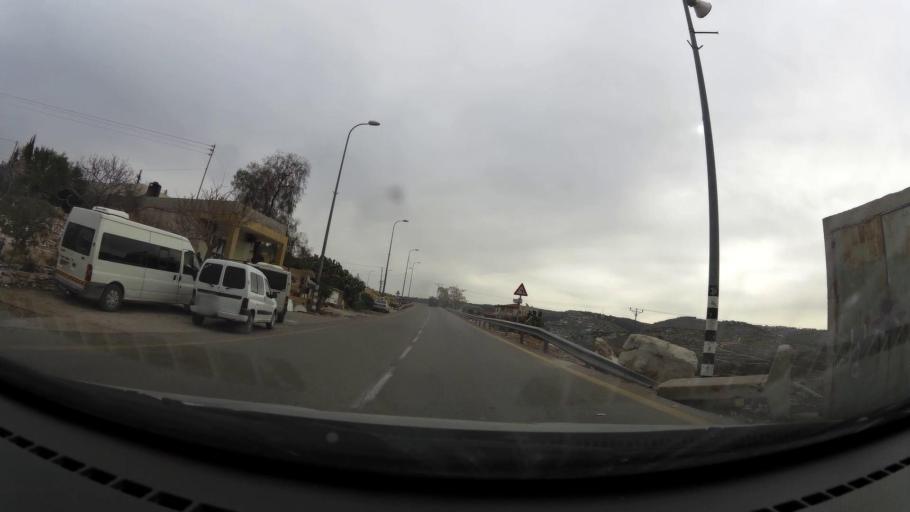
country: PS
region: West Bank
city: Surif
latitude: 31.6692
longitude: 35.0742
